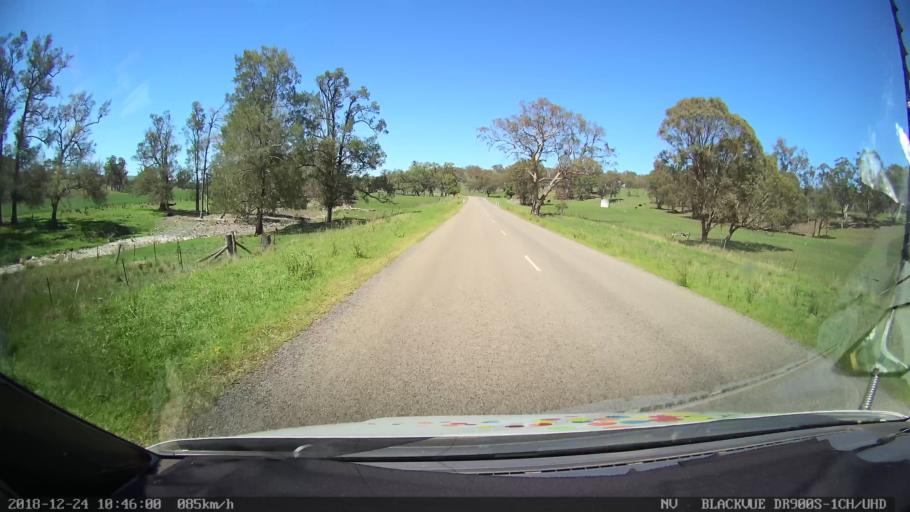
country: AU
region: New South Wales
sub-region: Upper Hunter Shire
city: Merriwa
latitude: -31.9083
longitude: 150.4316
